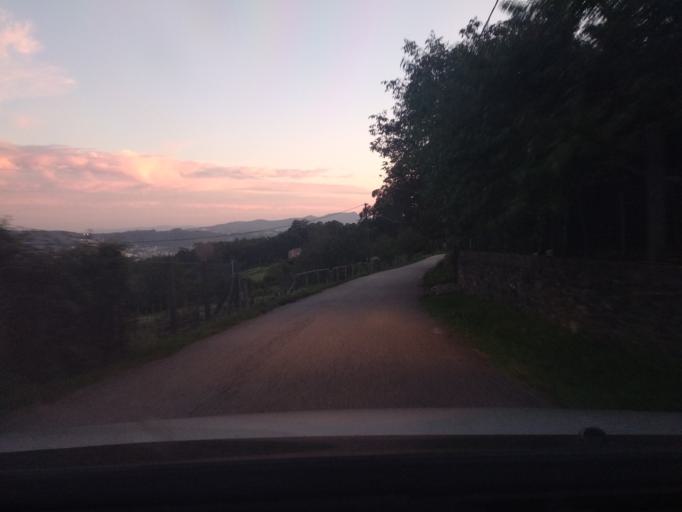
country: ES
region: Galicia
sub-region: Provincia de Pontevedra
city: Moana
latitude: 42.3062
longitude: -8.6987
